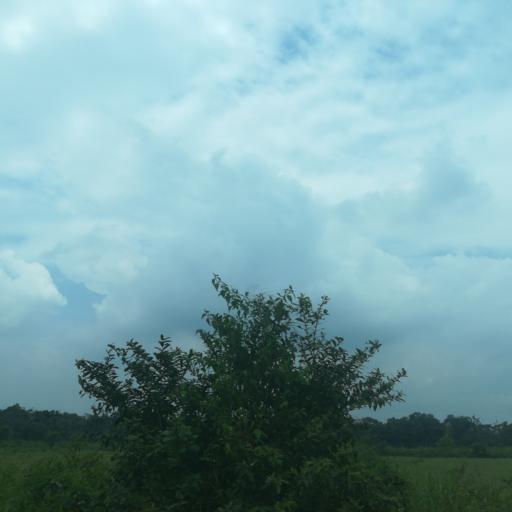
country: NG
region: Lagos
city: Ejirin
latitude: 6.6701
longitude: 3.7964
